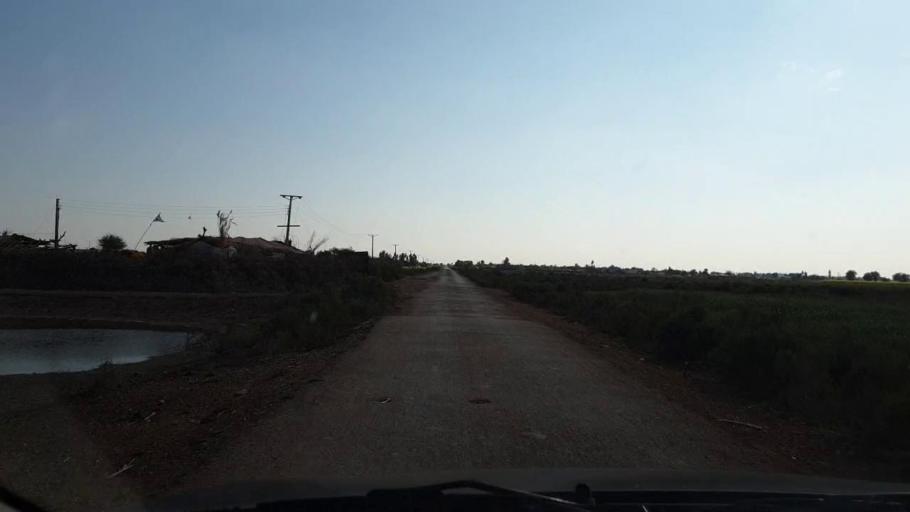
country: PK
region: Sindh
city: Sinjhoro
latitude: 25.9979
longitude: 68.8394
